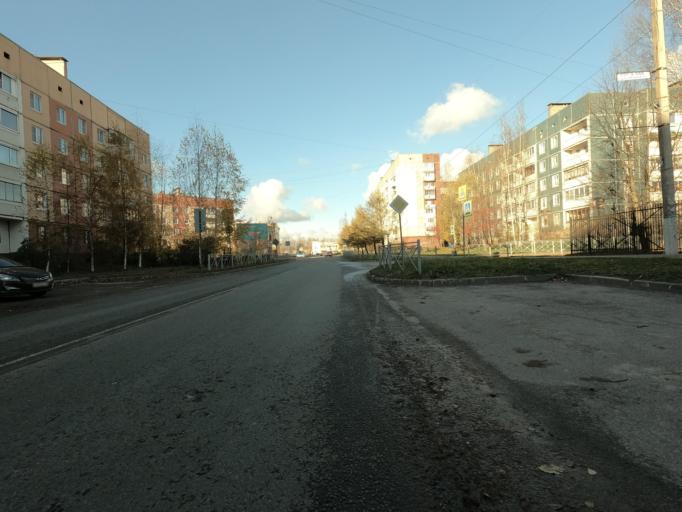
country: RU
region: Leningrad
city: Vsevolozhsk
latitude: 60.0301
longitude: 30.6297
